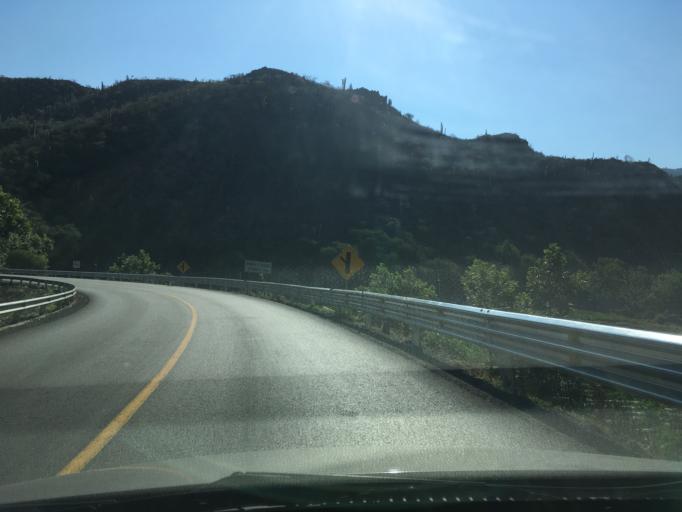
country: MX
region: Hidalgo
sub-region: San Agustin Metzquititlan
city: Mezquititlan
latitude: 20.4674
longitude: -98.6692
